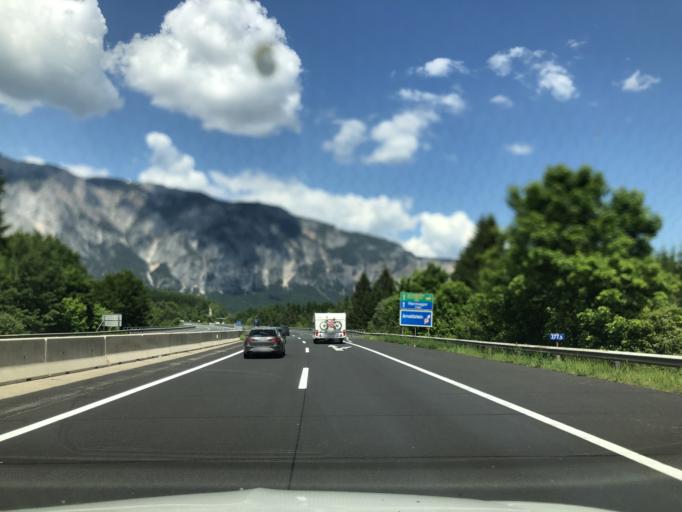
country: AT
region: Carinthia
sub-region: Politischer Bezirk Villach Land
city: Hohenthurn
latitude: 46.5449
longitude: 13.6794
